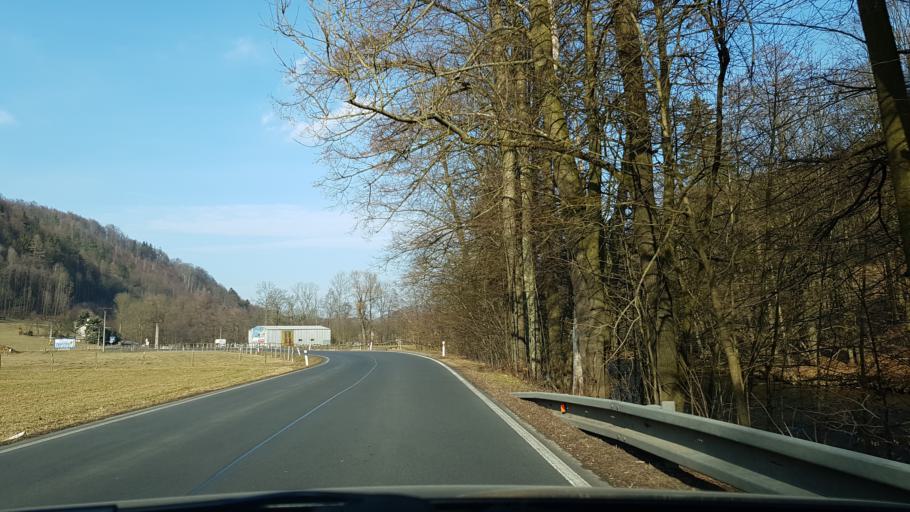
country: CZ
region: Olomoucky
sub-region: Okres Sumperk
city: Hanusovice
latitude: 50.0515
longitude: 16.9170
